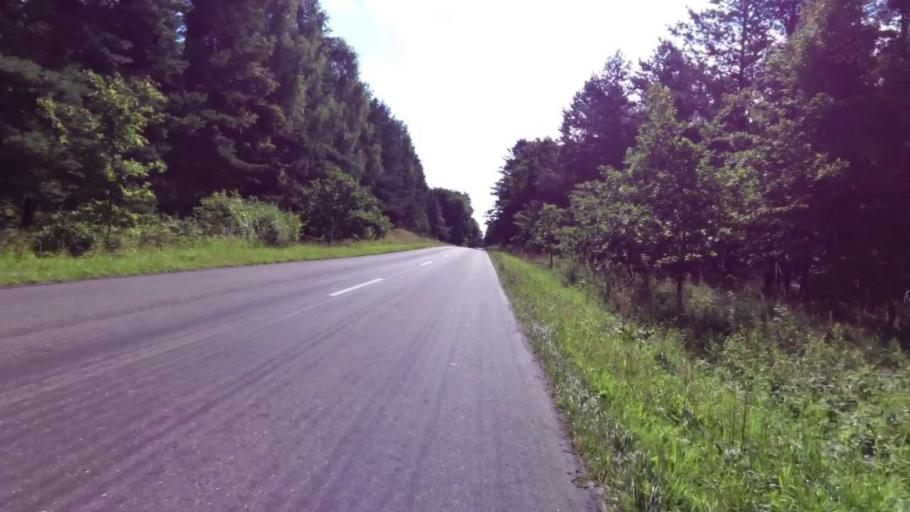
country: PL
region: West Pomeranian Voivodeship
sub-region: Powiat stargardzki
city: Dobrzany
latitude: 53.3679
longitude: 15.3920
